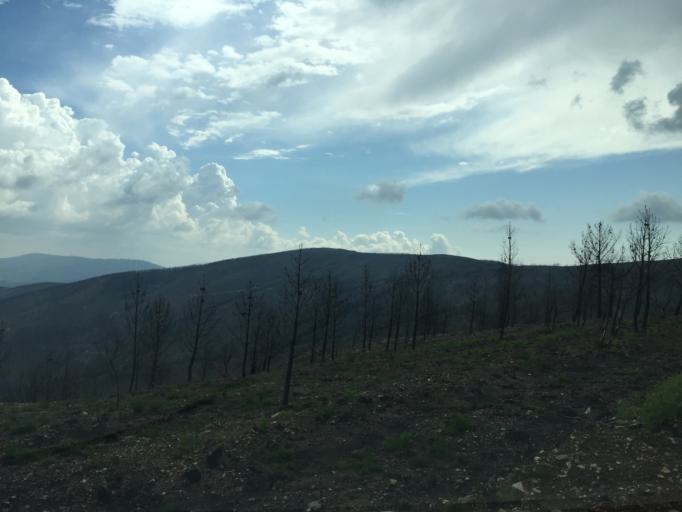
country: PT
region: Coimbra
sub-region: Arganil
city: Arganil
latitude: 40.1852
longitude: -7.9828
